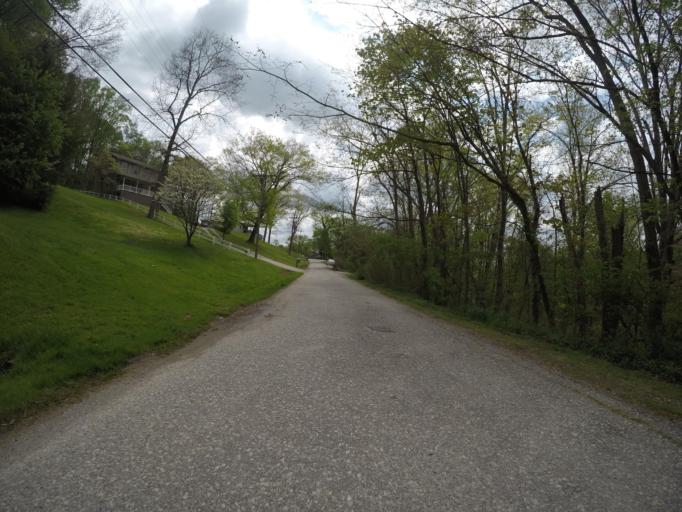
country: US
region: West Virginia
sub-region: Kanawha County
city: Charleston
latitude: 38.3884
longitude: -81.6043
